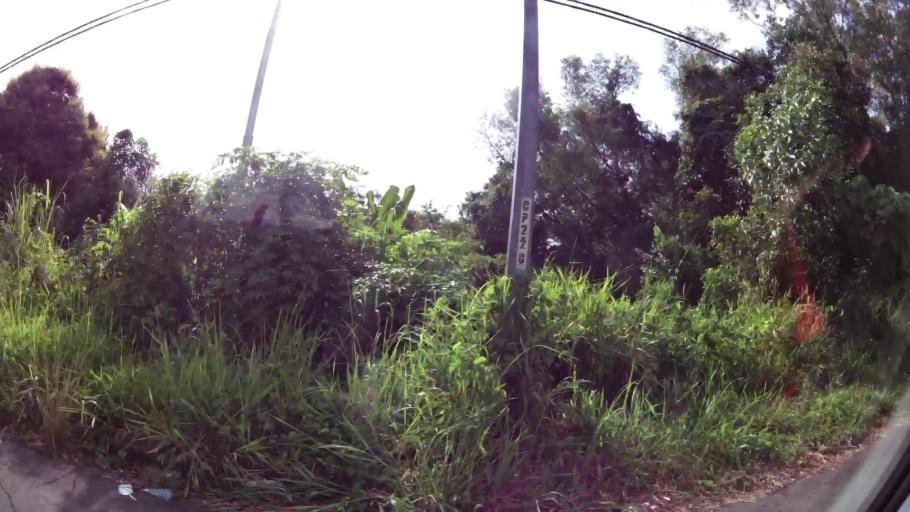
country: BN
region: Brunei and Muara
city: Bandar Seri Begawan
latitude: 4.9617
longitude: 114.9630
